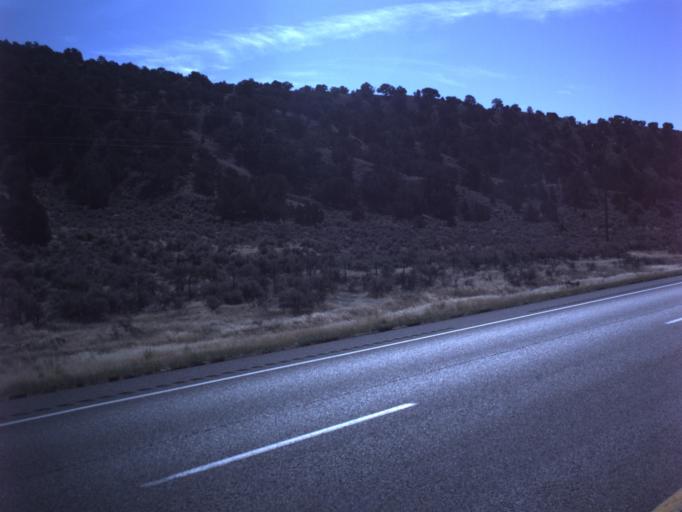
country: US
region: Utah
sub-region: Sanpete County
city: Gunnison
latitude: 39.3565
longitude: -111.9297
